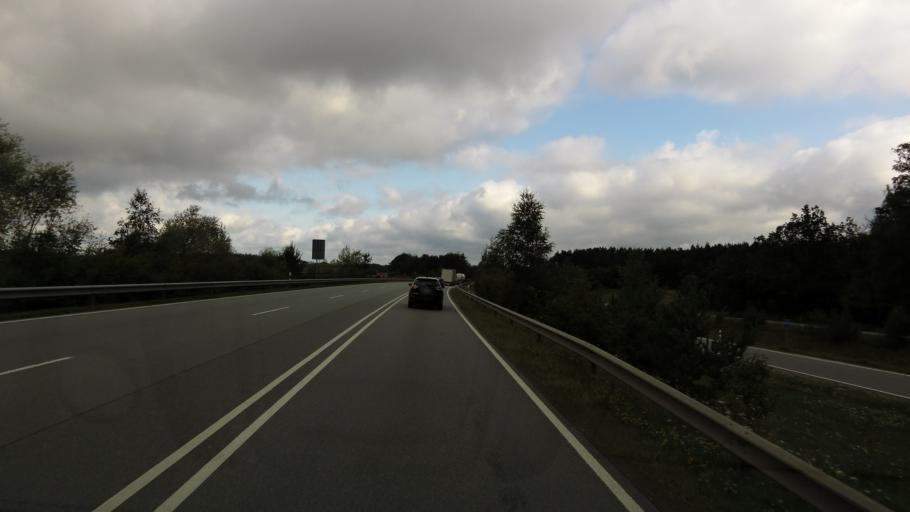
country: DE
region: Bavaria
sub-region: Upper Palatinate
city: Traitsching
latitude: 49.1745
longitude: 12.6513
